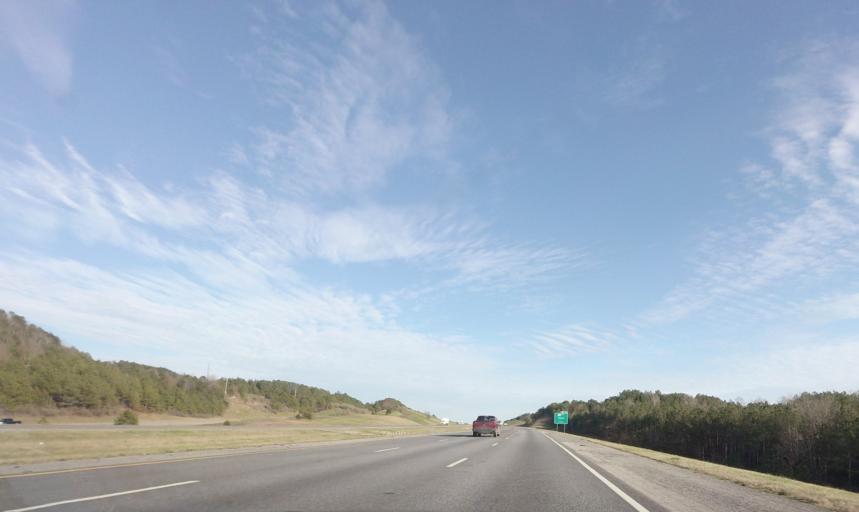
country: US
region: Alabama
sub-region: Walker County
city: Jasper
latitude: 33.8579
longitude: -87.3751
